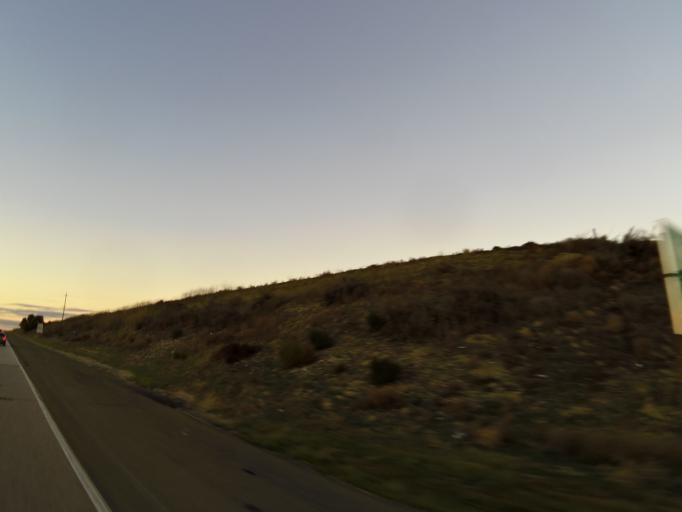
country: US
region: California
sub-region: Monterey County
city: King City
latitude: 36.1276
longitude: -121.0269
